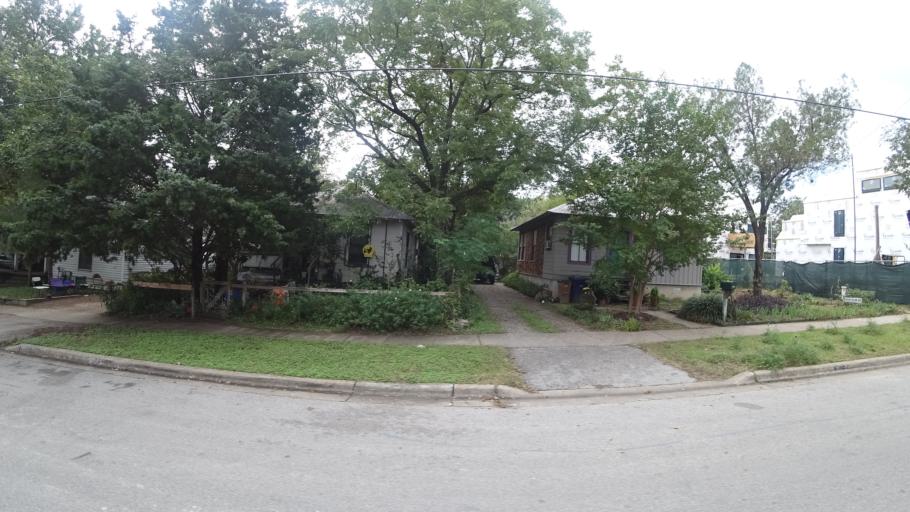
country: US
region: Texas
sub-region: Travis County
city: Austin
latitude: 30.2502
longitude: -97.7574
